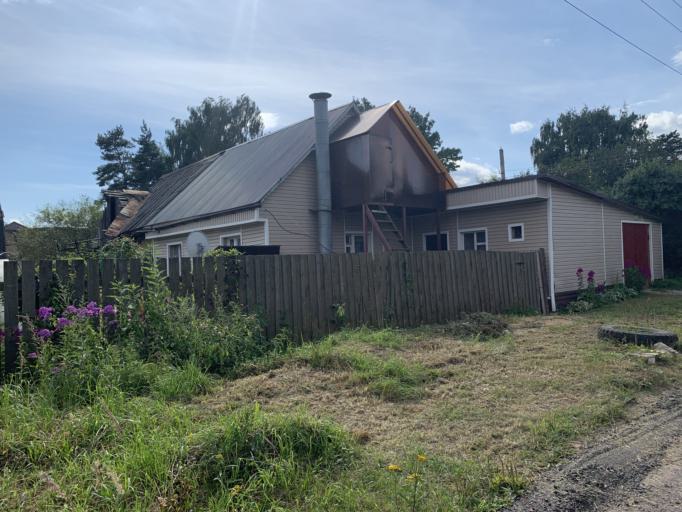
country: RU
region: Moskovskaya
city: Cherkizovo
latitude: 55.9876
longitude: 37.8017
